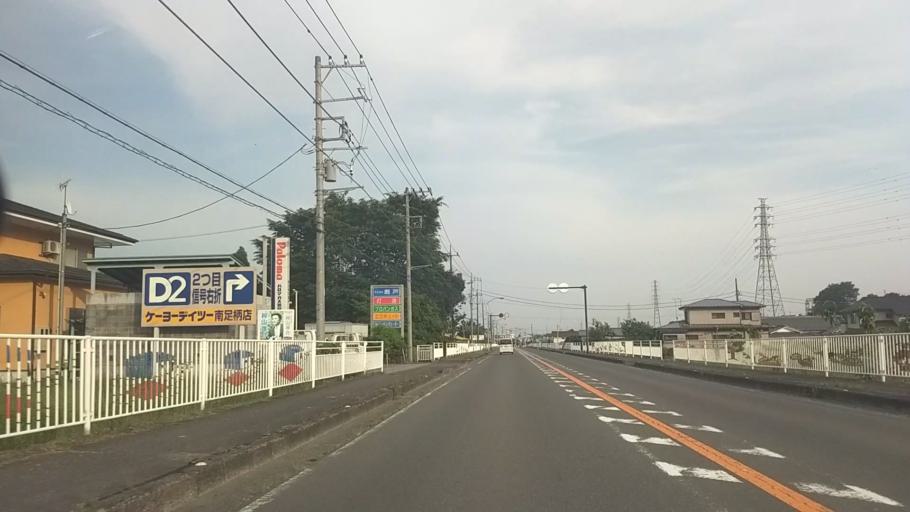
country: JP
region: Kanagawa
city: Odawara
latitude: 35.3403
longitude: 139.1028
